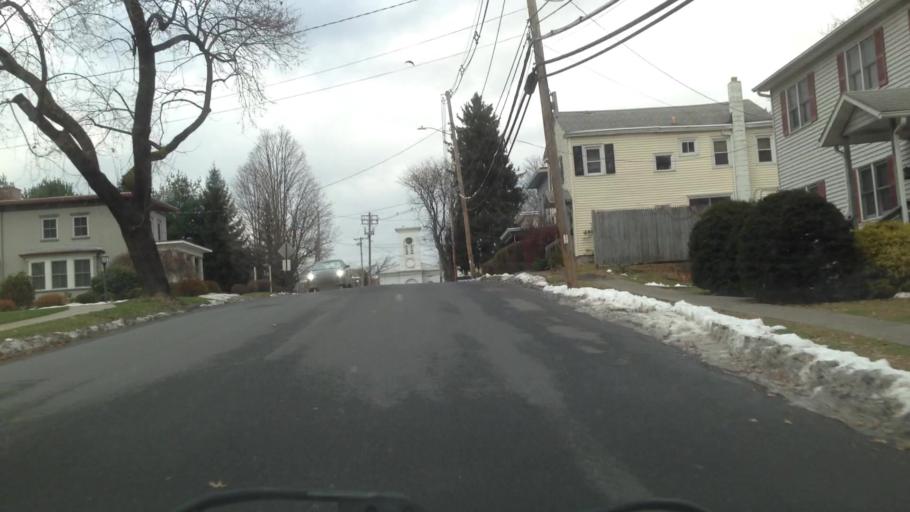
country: US
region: New York
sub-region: Ulster County
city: Saugerties
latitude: 42.0753
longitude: -73.9541
